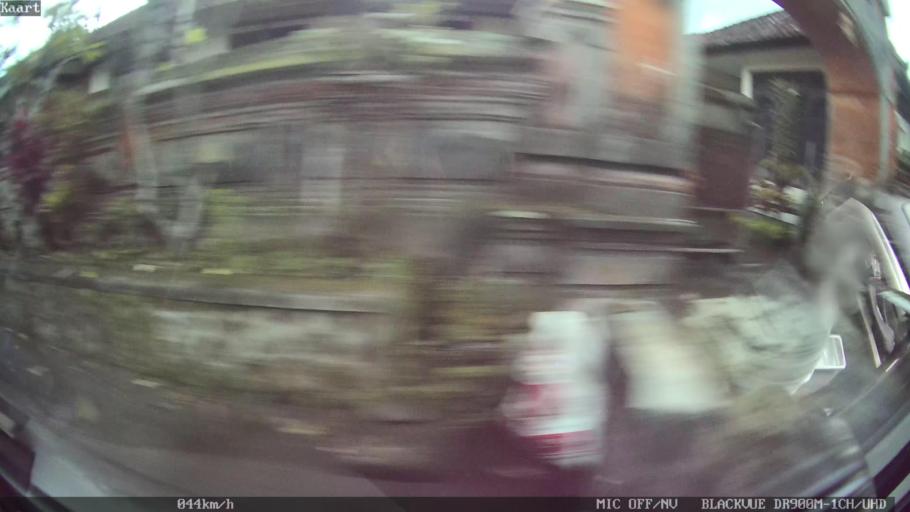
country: ID
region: Bali
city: Banjar Tebongkang
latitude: -8.5249
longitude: 115.2336
